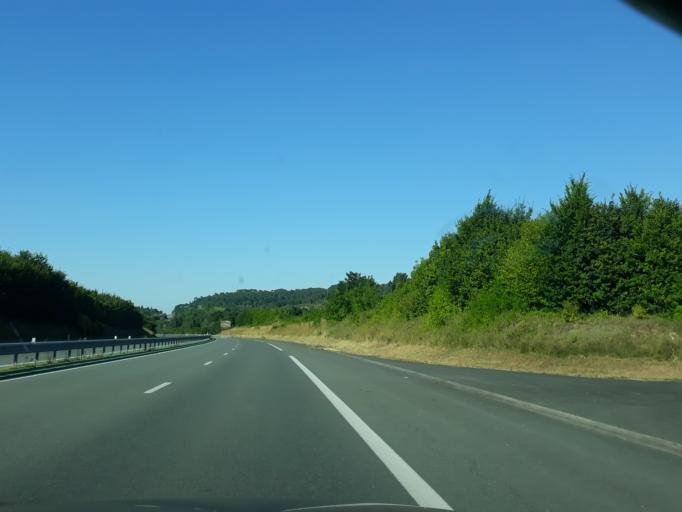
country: FR
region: Aquitaine
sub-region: Departement de la Dordogne
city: Neuvic
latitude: 45.0834
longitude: 0.4652
